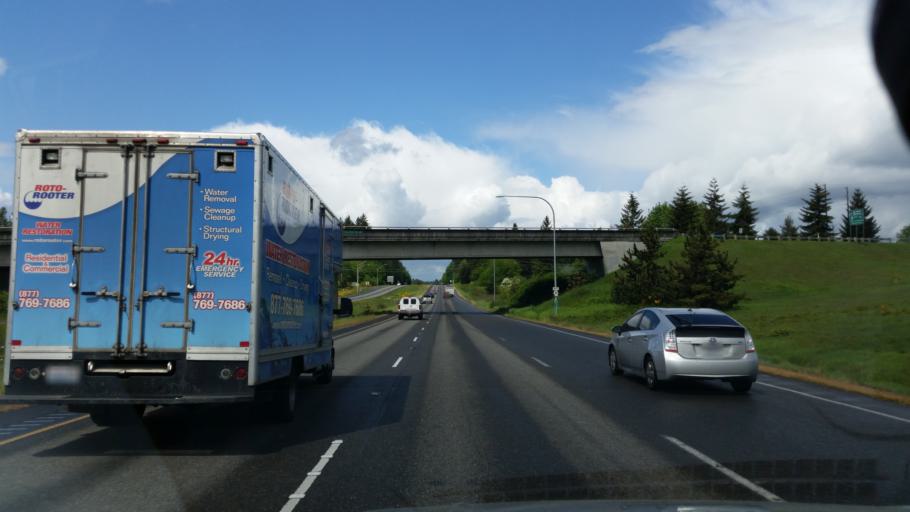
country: US
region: Washington
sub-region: Pierce County
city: Gig Harbor
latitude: 47.3203
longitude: -122.5896
